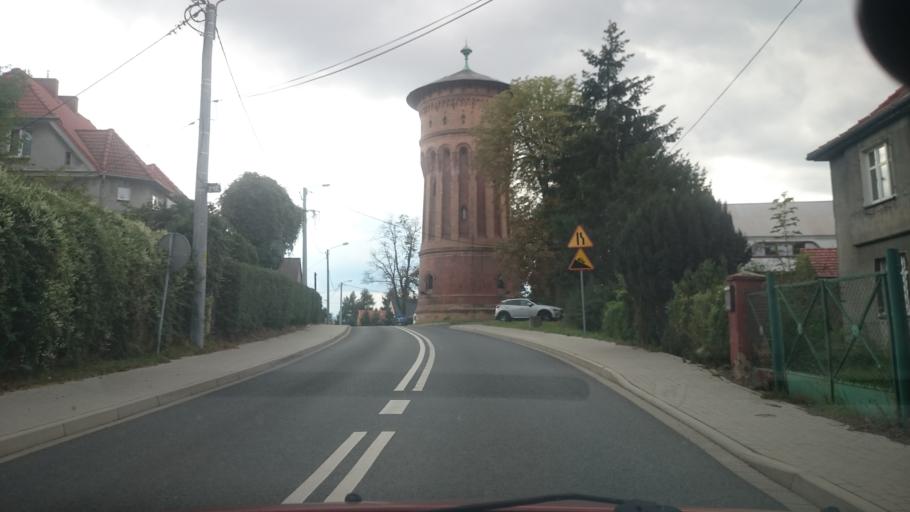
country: PL
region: Lower Silesian Voivodeship
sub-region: Powiat zabkowicki
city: Zabkowice Slaskie
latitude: 50.5903
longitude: 16.8212
